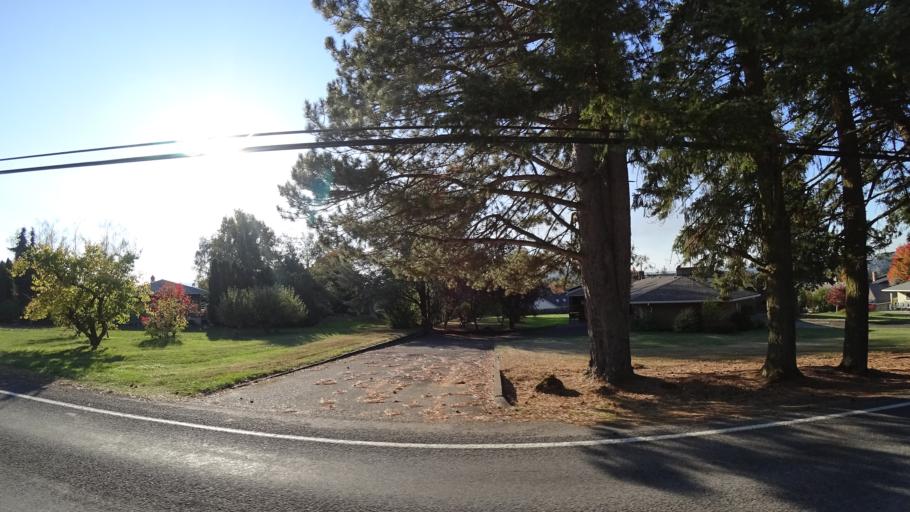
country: US
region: Oregon
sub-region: Multnomah County
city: Gresham
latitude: 45.4781
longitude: -122.4483
